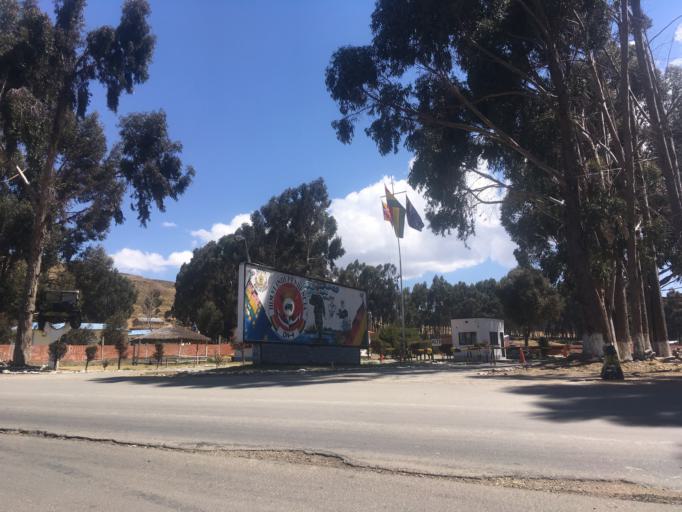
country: BO
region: La Paz
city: Huatajata
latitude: -16.1896
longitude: -68.7480
